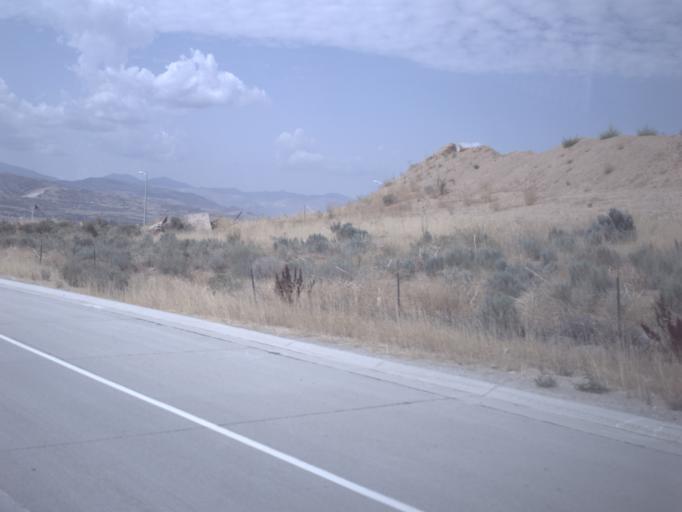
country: US
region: Utah
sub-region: Utah County
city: Lehi
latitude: 40.4326
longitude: -111.8718
